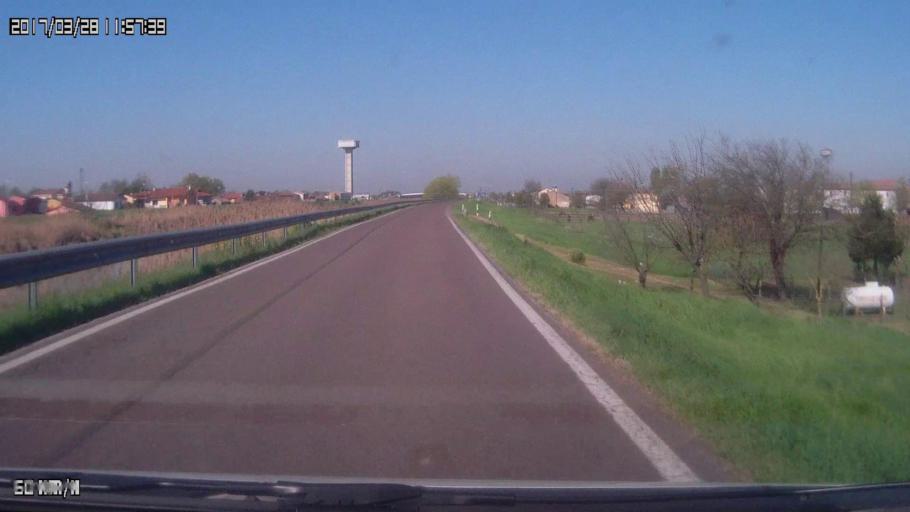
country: IT
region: Veneto
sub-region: Provincia di Venezia
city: Boscochiaro
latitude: 45.1371
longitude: 12.1240
